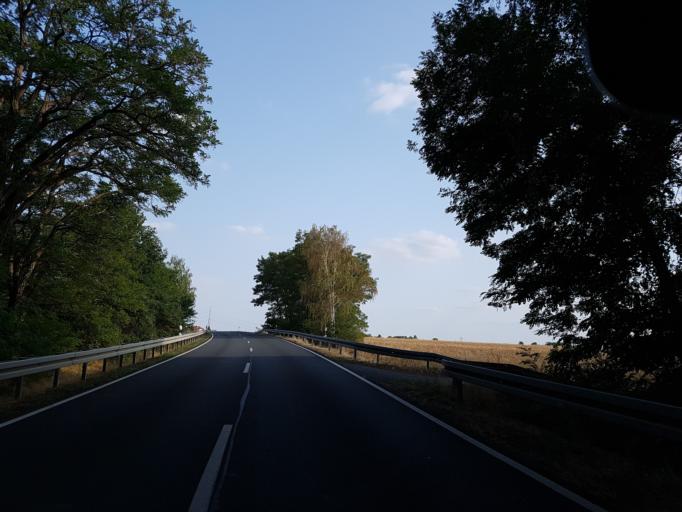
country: DE
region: Saxony-Anhalt
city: Pretzsch
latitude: 51.6729
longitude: 12.8334
